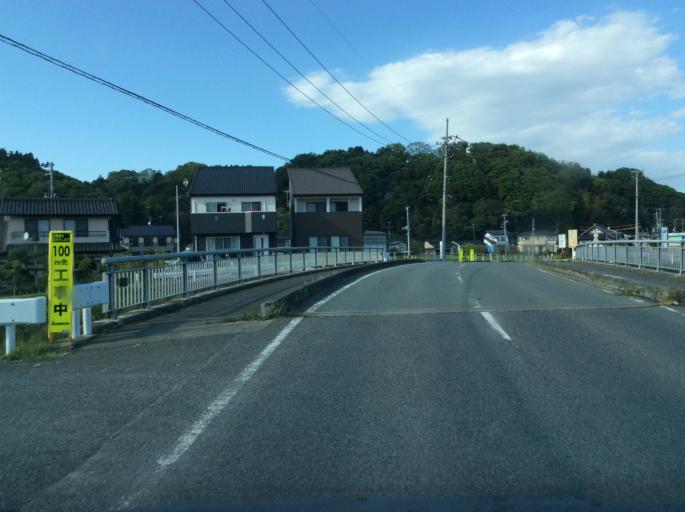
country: JP
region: Fukushima
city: Iwaki
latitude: 36.9850
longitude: 140.8460
